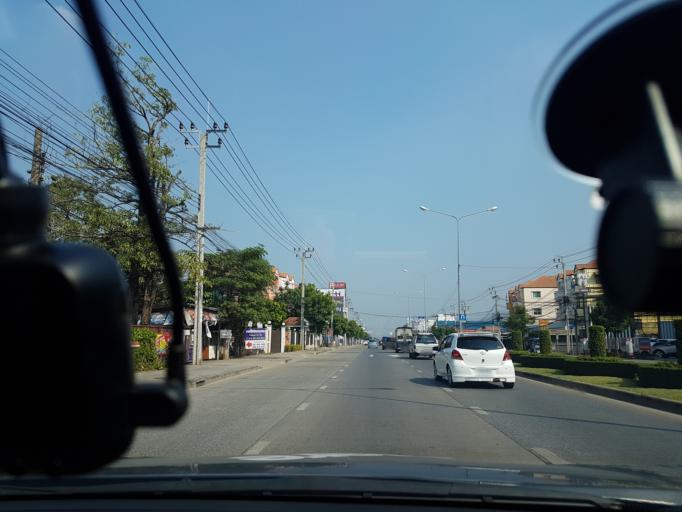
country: TH
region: Bangkok
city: Khlong Sam Wa
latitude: 13.8609
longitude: 100.7112
